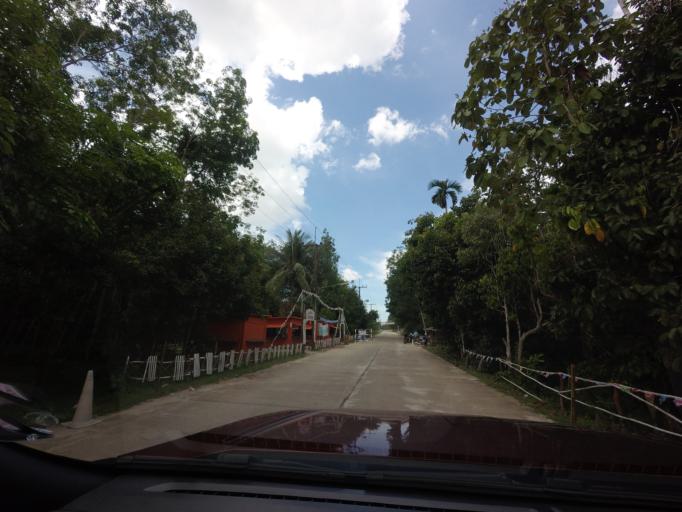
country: TH
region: Narathiwat
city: Bacho
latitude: 6.4847
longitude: 101.6575
